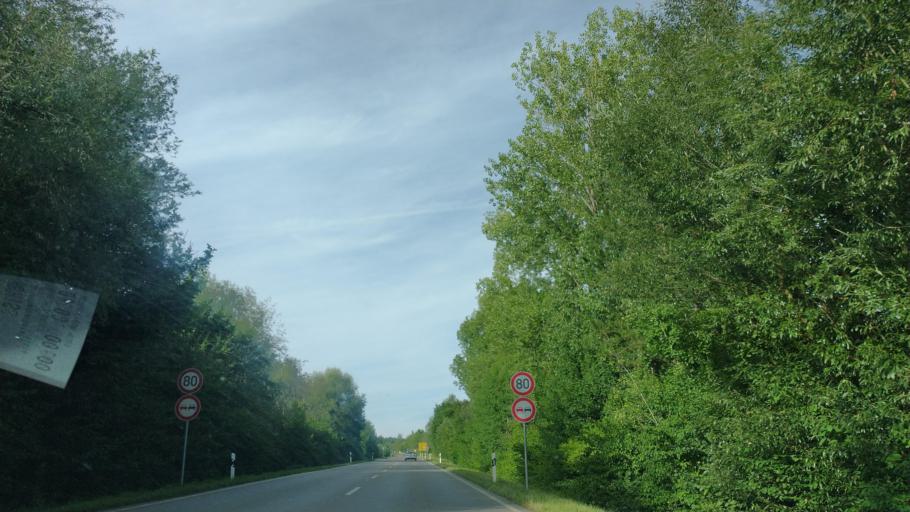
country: DE
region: Baden-Wuerttemberg
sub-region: Tuebingen Region
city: Kressbronn am Bodensee
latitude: 47.6021
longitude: 9.5817
